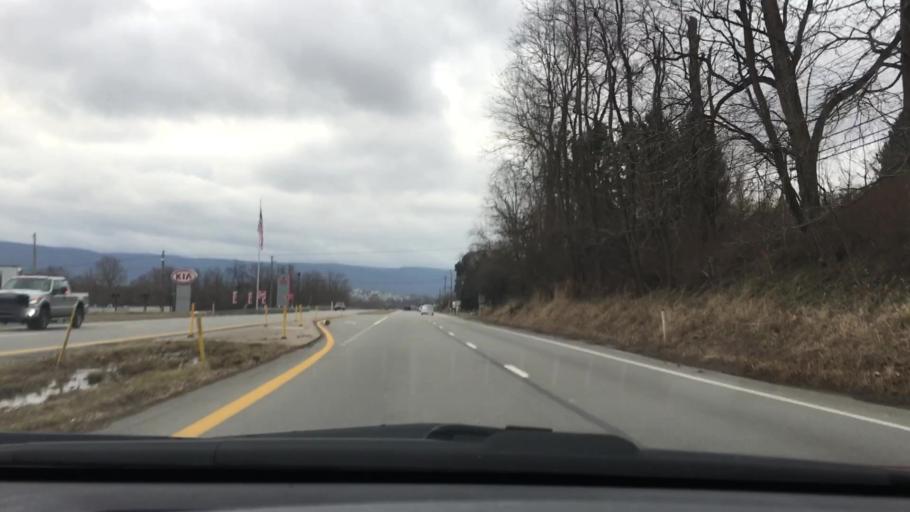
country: US
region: Pennsylvania
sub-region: Fayette County
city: Oliver
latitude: 39.9349
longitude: -79.7301
